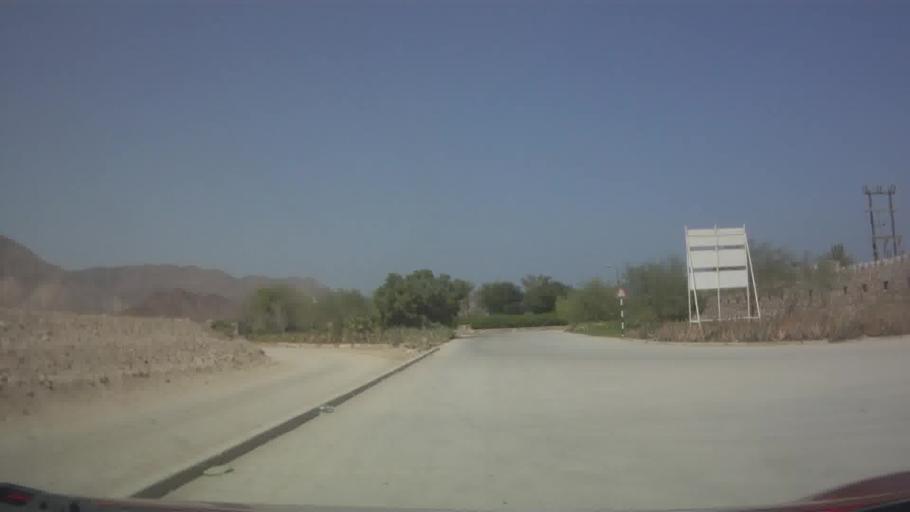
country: OM
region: Muhafazat Masqat
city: Muscat
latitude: 23.4126
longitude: 58.7851
